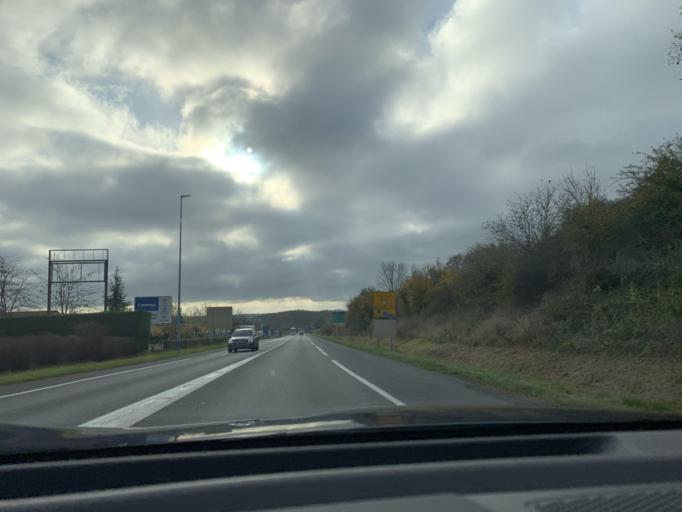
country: FR
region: Bourgogne
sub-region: Departement de Saone-et-Loire
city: Saint-Martin-Belle-Roche
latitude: 46.3629
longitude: 4.8422
